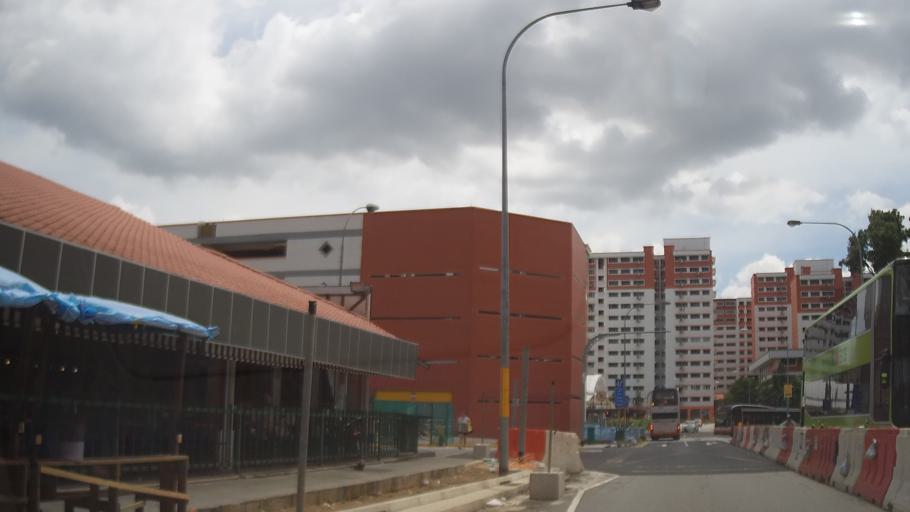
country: MY
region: Johor
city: Johor Bahru
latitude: 1.3850
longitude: 103.7430
